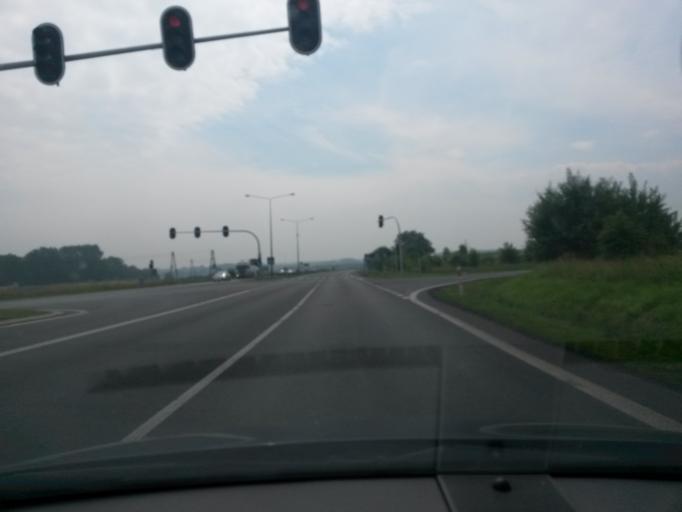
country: PL
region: Lodz Voivodeship
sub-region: Powiat piotrkowski
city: Wola Krzysztoporska
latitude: 51.3219
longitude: 19.5794
